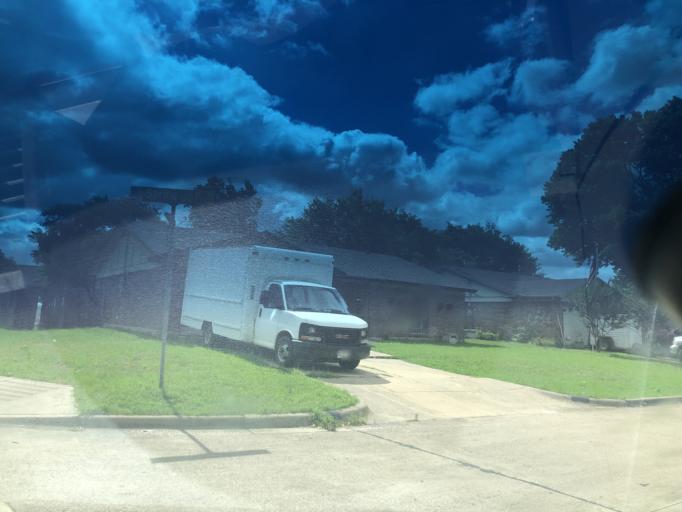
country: US
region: Texas
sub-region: Dallas County
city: Grand Prairie
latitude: 32.7071
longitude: -97.0390
